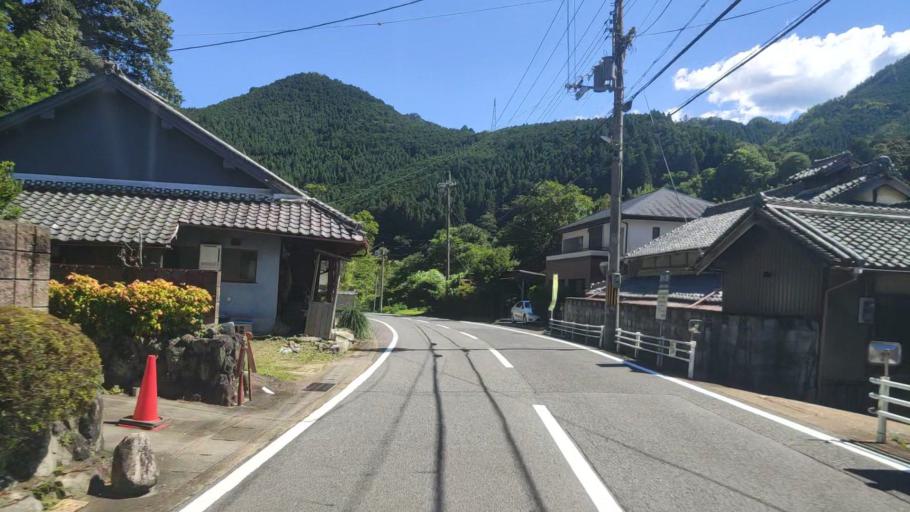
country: JP
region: Nara
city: Yoshino-cho
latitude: 34.3789
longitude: 135.9092
